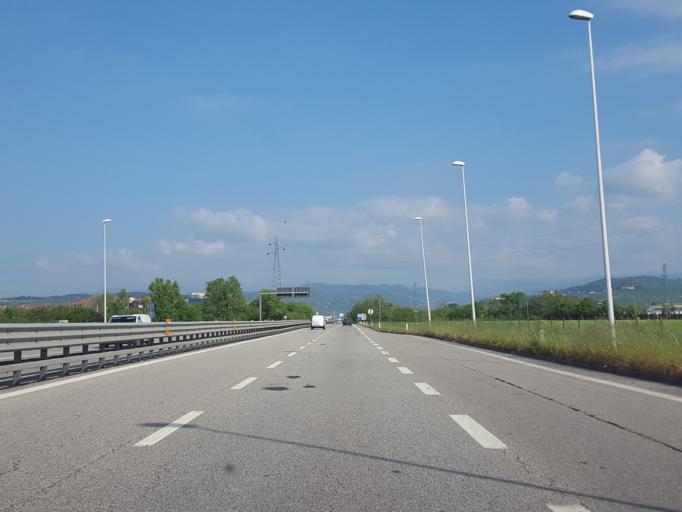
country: IT
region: Veneto
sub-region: Provincia di Verona
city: Montorio
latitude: 45.4313
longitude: 11.0632
